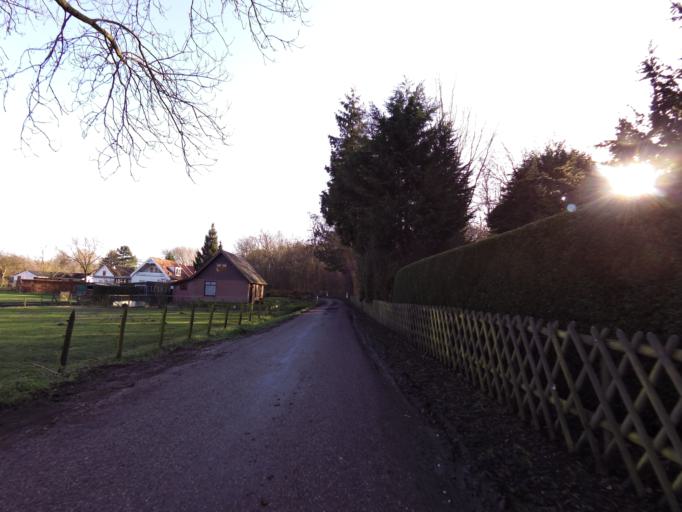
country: NL
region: South Holland
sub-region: Gemeente Hellevoetsluis
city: Nieuw-Helvoet
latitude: 51.8665
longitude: 4.0653
